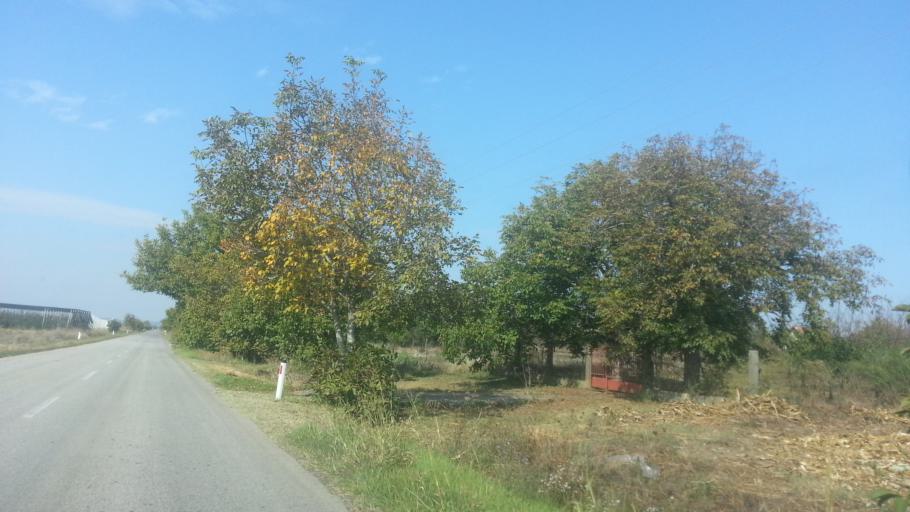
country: RS
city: Surduk
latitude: 45.0847
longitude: 20.3065
